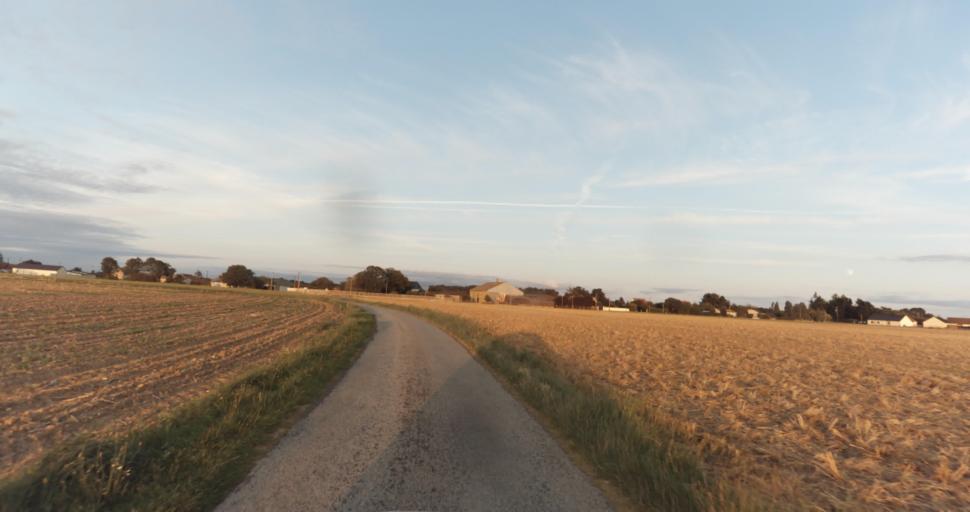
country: FR
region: Haute-Normandie
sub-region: Departement de l'Eure
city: La Madeleine-de-Nonancourt
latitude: 48.8723
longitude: 1.1818
